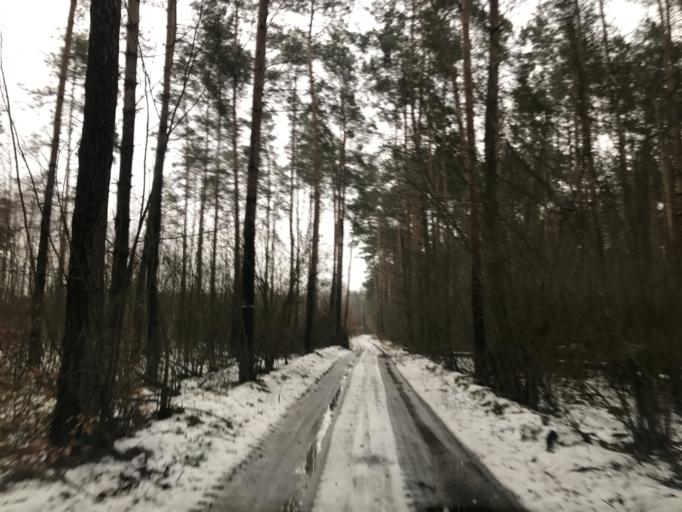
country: PL
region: Kujawsko-Pomorskie
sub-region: Powiat brodnicki
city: Bartniczka
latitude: 53.2841
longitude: 19.5798
